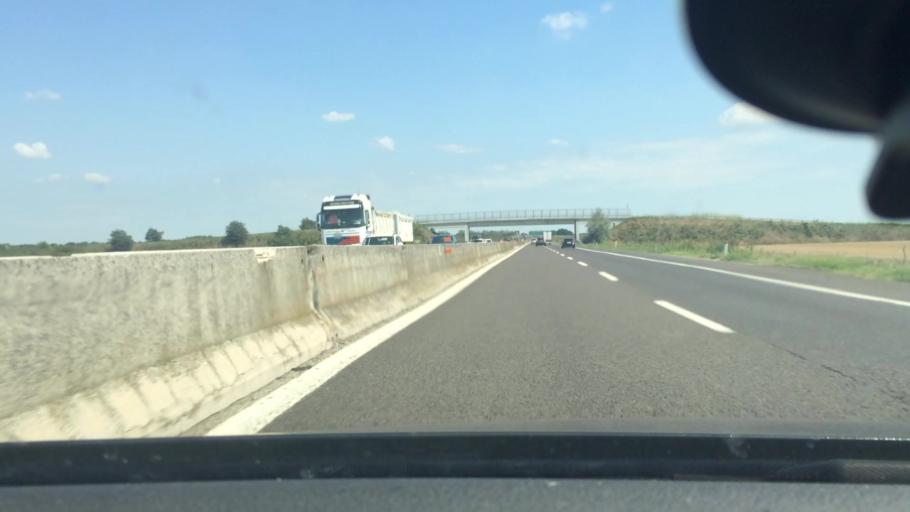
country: IT
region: Emilia-Romagna
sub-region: Provincia di Bologna
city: Altedo
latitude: 44.6768
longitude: 11.4709
